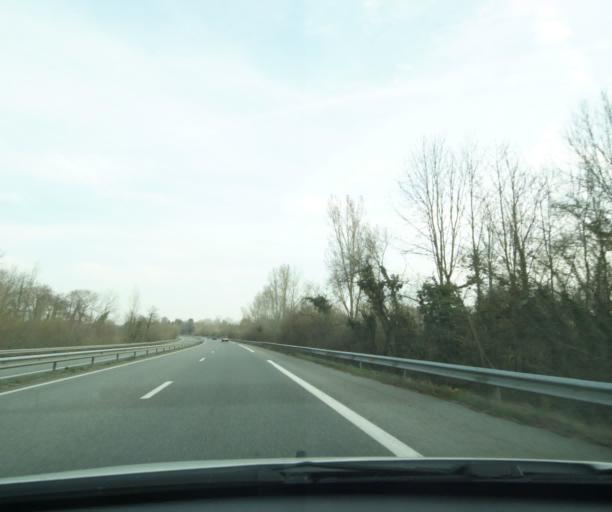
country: FR
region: Midi-Pyrenees
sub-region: Departement des Hautes-Pyrenees
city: Juillan
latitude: 43.2114
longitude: 0.0366
